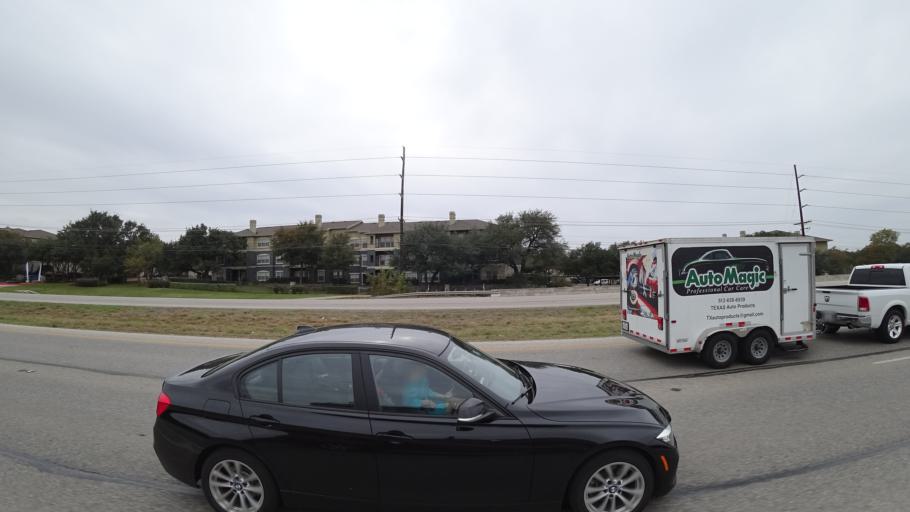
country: US
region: Texas
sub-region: Williamson County
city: Jollyville
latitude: 30.4519
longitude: -97.7494
